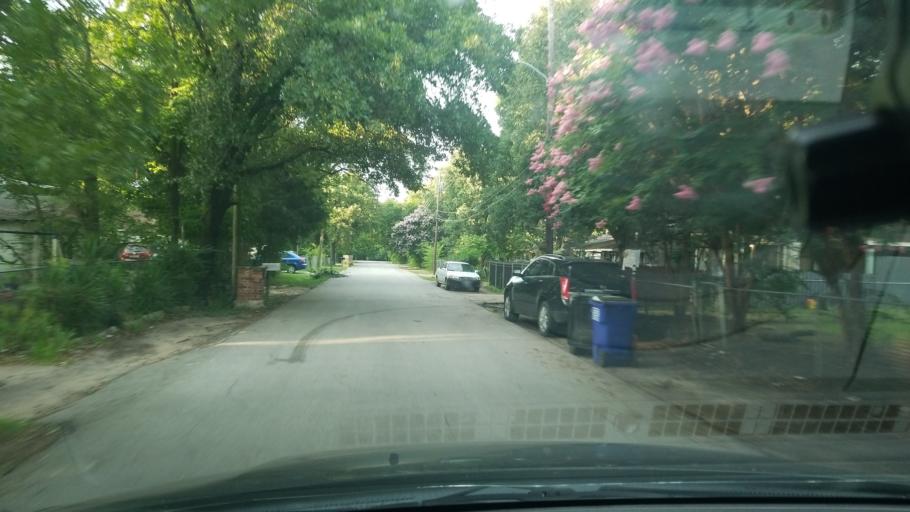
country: US
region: Texas
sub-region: Dallas County
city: Balch Springs
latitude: 32.7473
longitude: -96.6377
